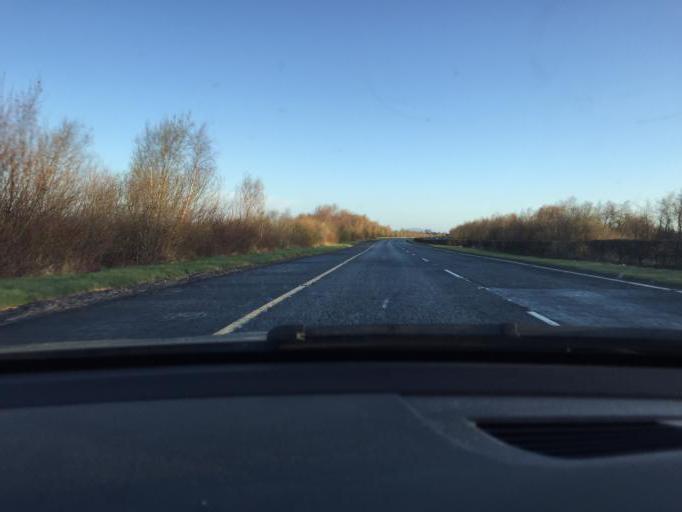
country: IE
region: Leinster
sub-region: Lu
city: Castlebellingham
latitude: 53.8782
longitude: -6.4299
